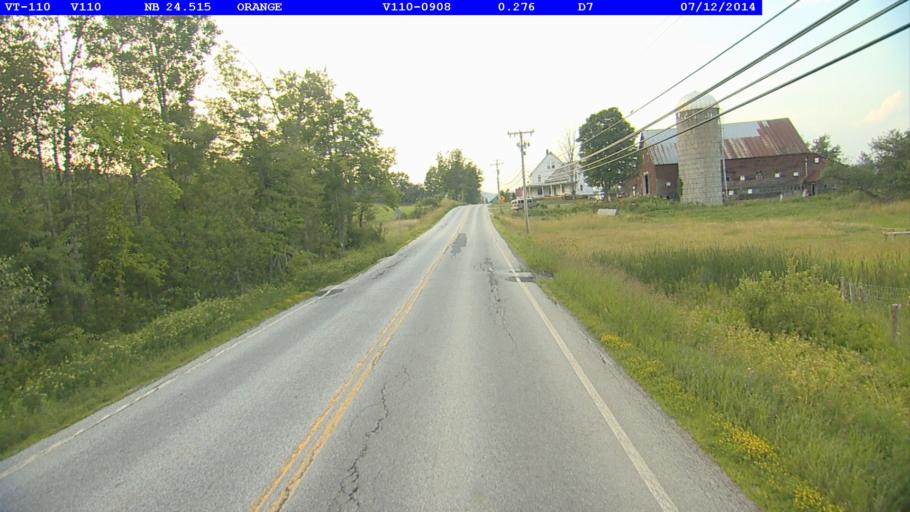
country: US
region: Vermont
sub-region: Washington County
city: South Barre
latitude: 44.1282
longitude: -72.4303
